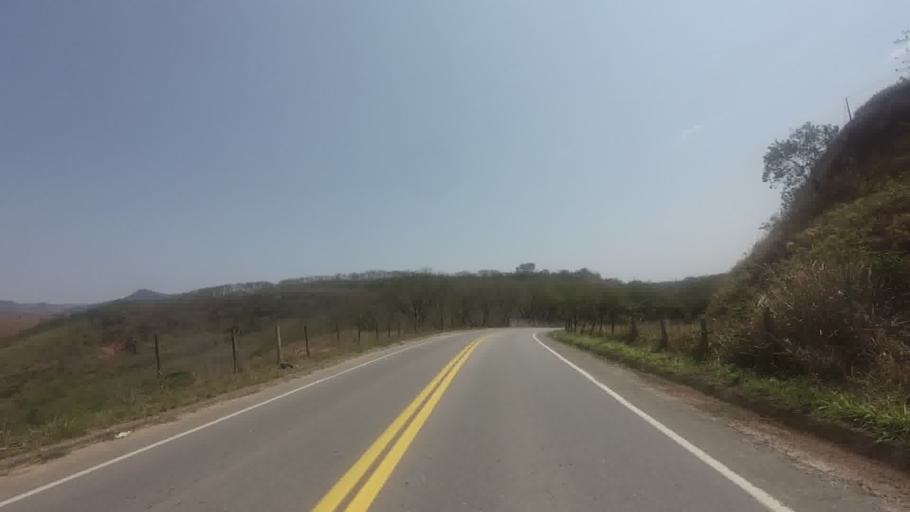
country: BR
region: Espirito Santo
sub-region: Cachoeiro De Itapemirim
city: Cachoeiro de Itapemirim
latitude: -20.8564
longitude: -41.0845
